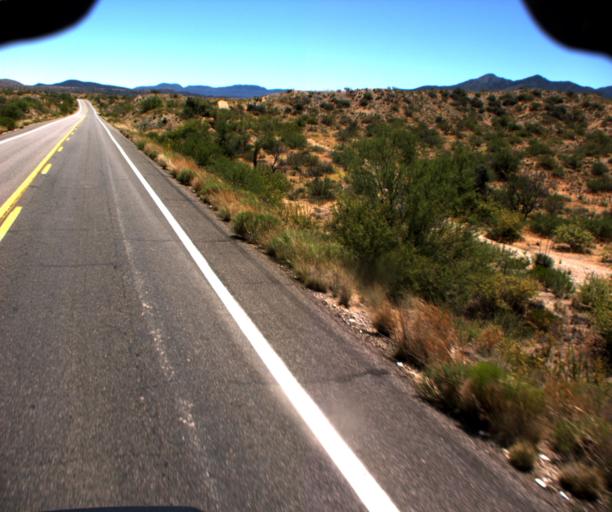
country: US
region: Arizona
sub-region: Gila County
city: Globe
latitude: 33.3632
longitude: -110.7365
